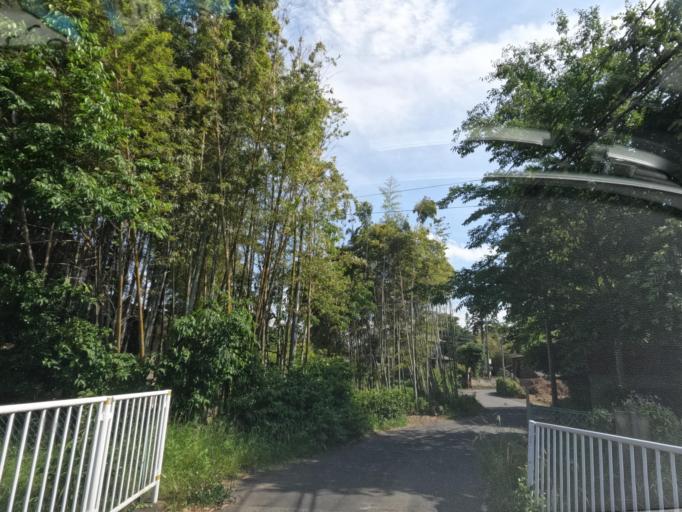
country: JP
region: Saitama
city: Kumagaya
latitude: 36.1039
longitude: 139.3835
